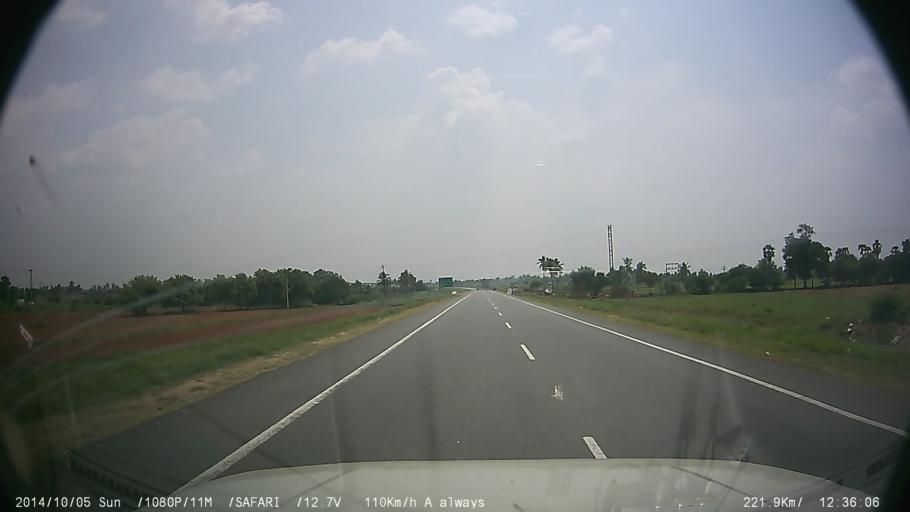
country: IN
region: Tamil Nadu
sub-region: Cuddalore
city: Vriddhachalam
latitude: 11.6900
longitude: 79.2690
